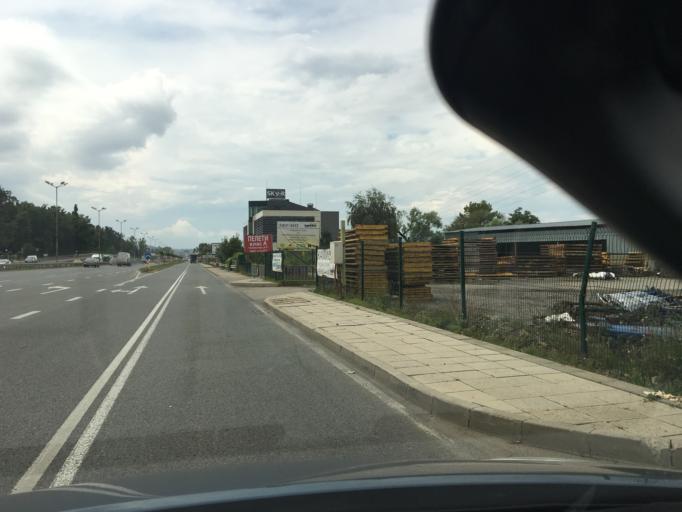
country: BG
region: Sofia-Capital
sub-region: Stolichna Obshtina
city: Sofia
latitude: 42.6458
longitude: 23.3028
